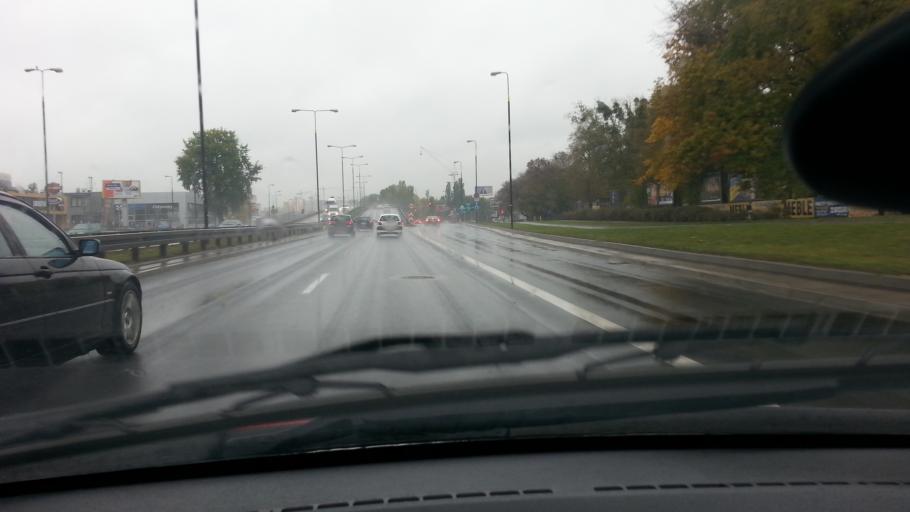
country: PL
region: Masovian Voivodeship
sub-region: Warszawa
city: Wola
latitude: 52.2403
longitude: 20.9568
